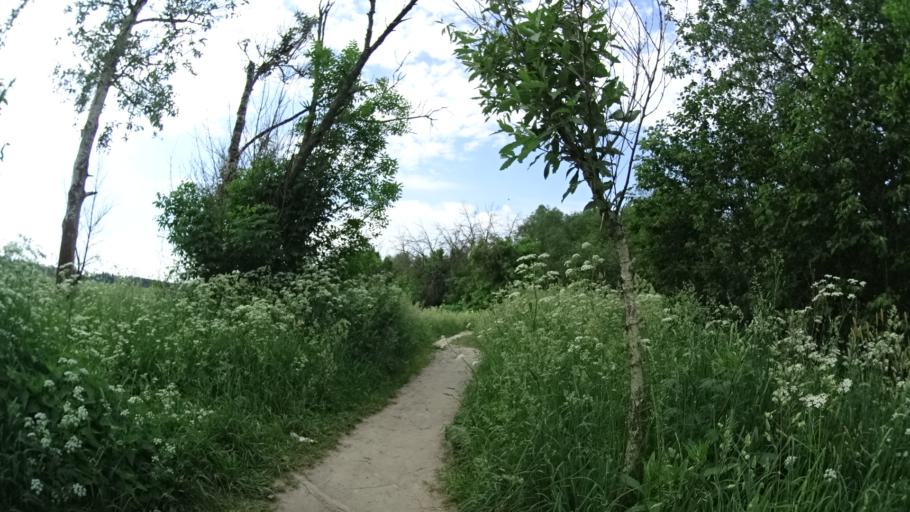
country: RU
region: Moskovskaya
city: Zelenogradskiy
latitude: 56.0853
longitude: 37.9089
